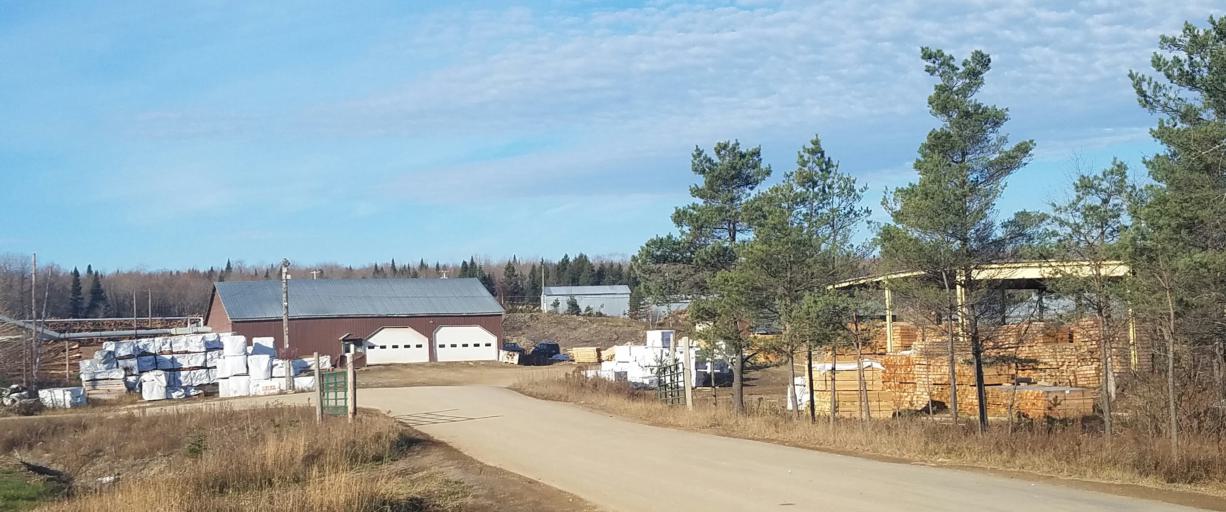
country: US
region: Maine
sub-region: Aroostook County
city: Hodgdon
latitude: 46.1154
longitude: -68.1614
